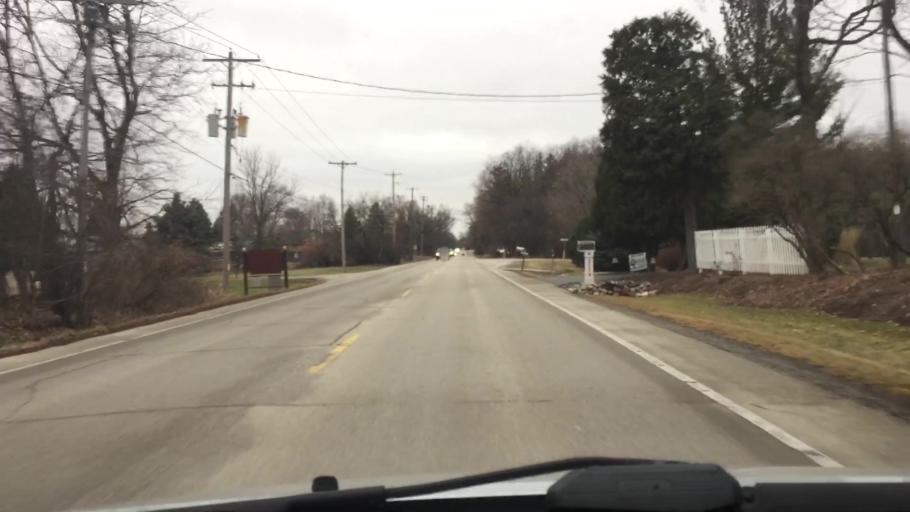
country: US
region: Wisconsin
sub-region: Waukesha County
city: Delafield
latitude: 43.0789
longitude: -88.4035
